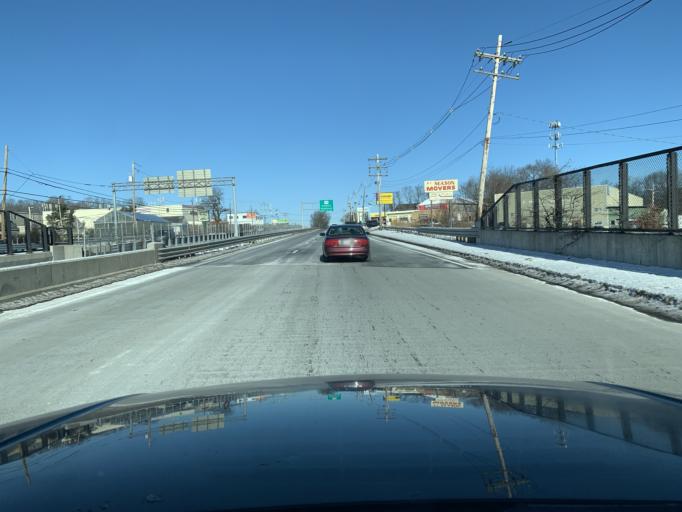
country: US
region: Massachusetts
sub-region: Essex County
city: South Peabody
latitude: 42.5482
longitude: -70.9832
